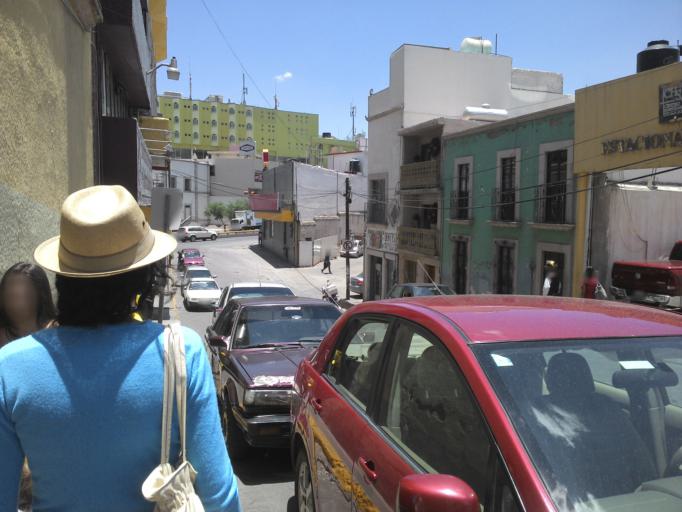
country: MX
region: Zacatecas
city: Zacatecas
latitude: 22.7699
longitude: -102.5701
